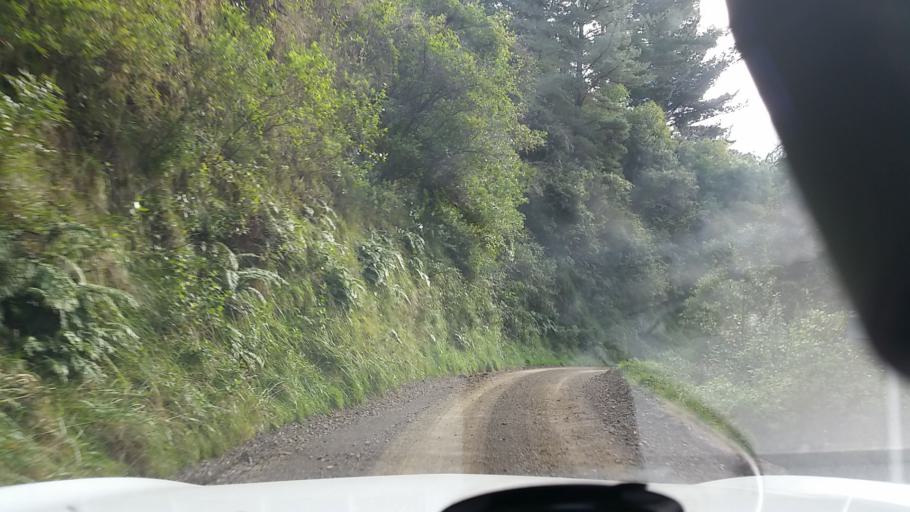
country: NZ
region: Hawke's Bay
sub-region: Napier City
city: Napier
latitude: -39.0926
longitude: 176.8706
